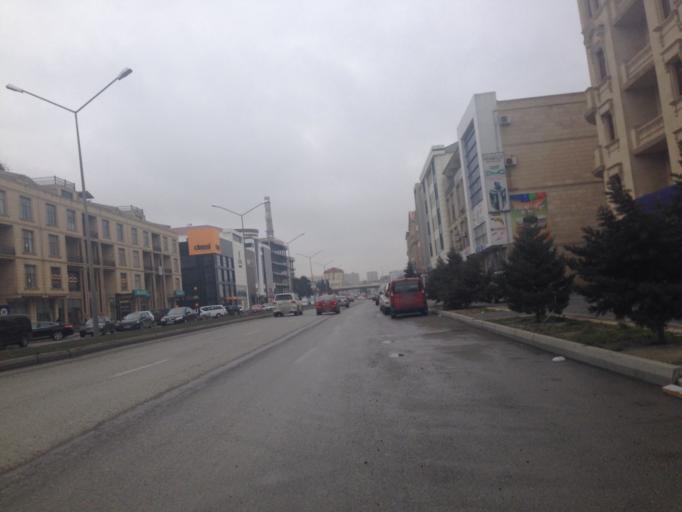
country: AZ
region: Baki
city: Baku
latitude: 40.4126
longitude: 49.8615
